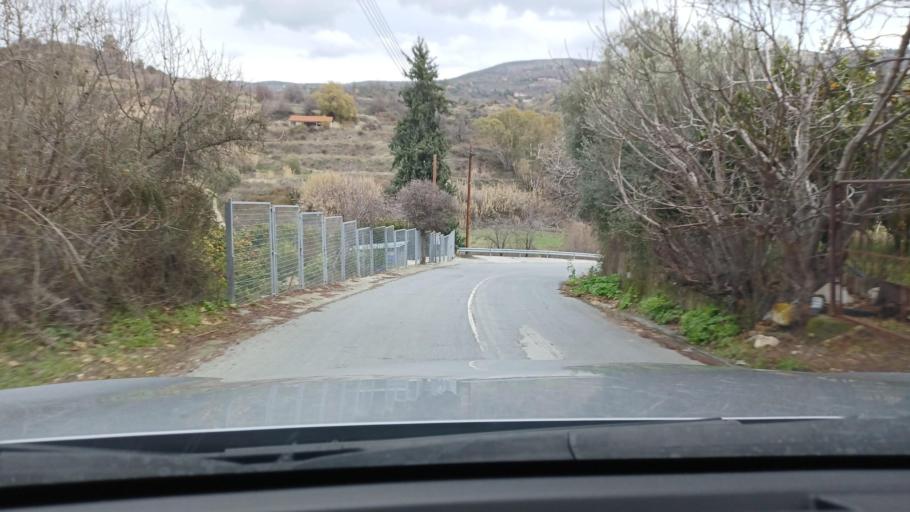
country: CY
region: Limassol
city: Pelendri
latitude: 34.8163
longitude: 32.9025
